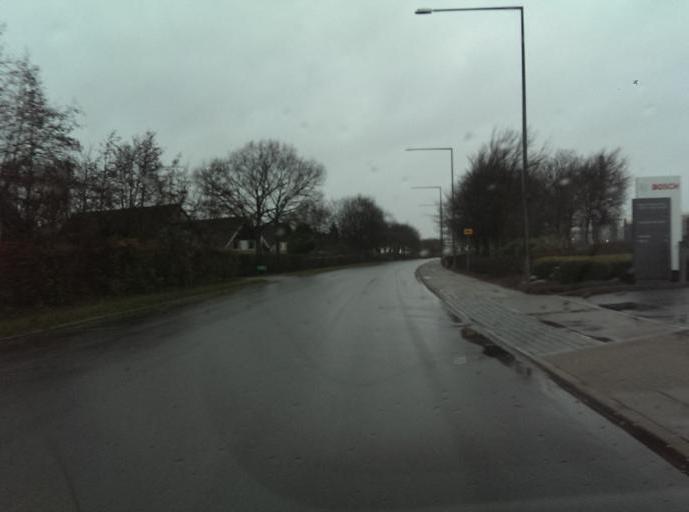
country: DK
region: South Denmark
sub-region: Esbjerg Kommune
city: Esbjerg
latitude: 55.4831
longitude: 8.4953
